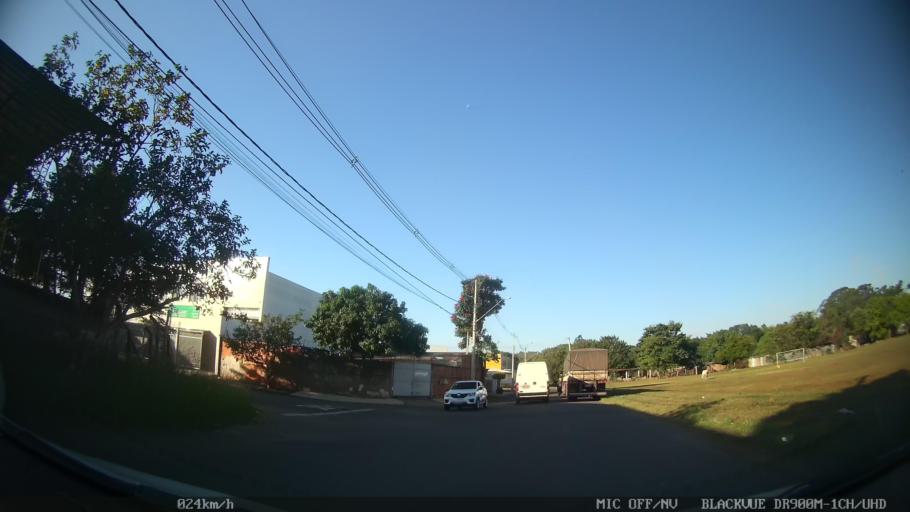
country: BR
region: Sao Paulo
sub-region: Nova Odessa
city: Nova Odessa
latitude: -22.7753
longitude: -47.2890
